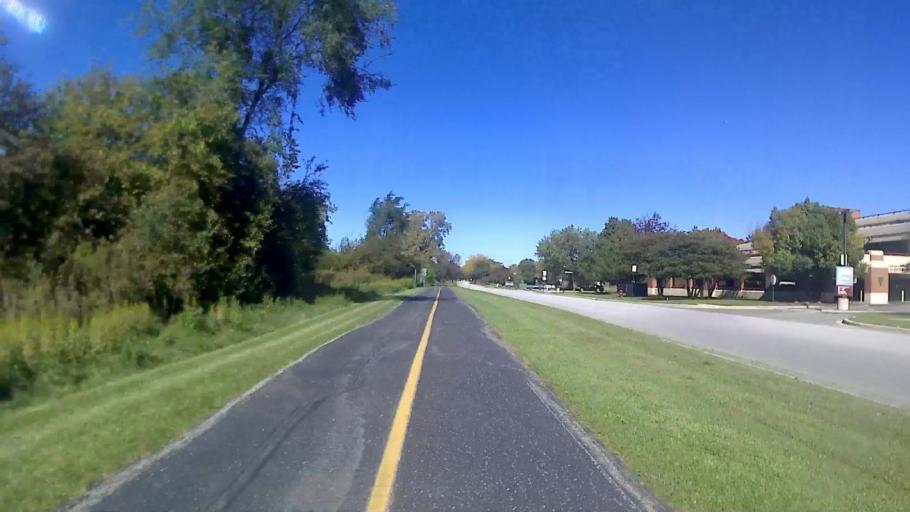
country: US
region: Illinois
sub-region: DuPage County
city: Itasca
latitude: 42.0057
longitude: -88.0186
